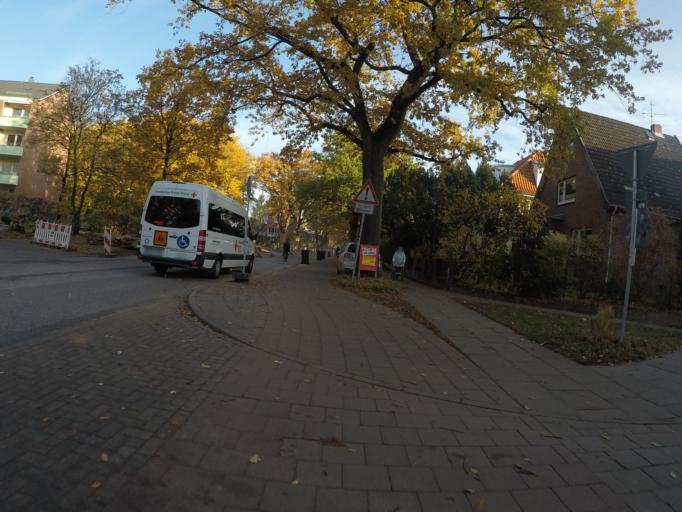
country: DE
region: Hamburg
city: Hamburg-Nord
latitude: 53.5887
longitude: 9.9577
